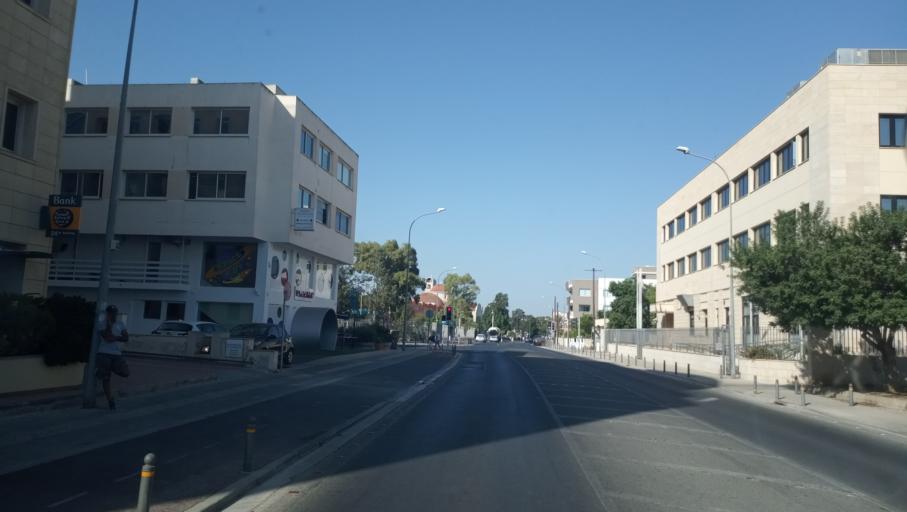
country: CY
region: Lefkosia
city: Nicosia
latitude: 35.1495
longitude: 33.3929
